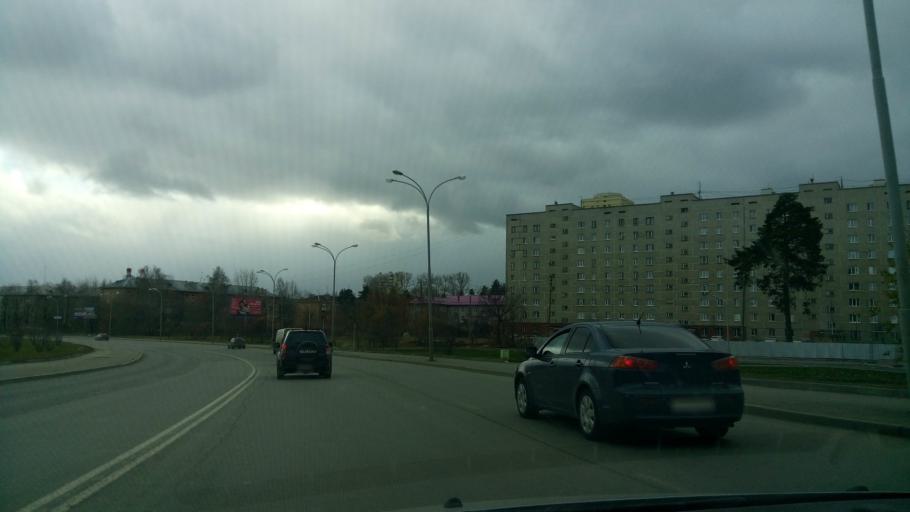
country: RU
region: Sverdlovsk
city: Shuvakish
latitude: 56.8763
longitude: 60.5260
